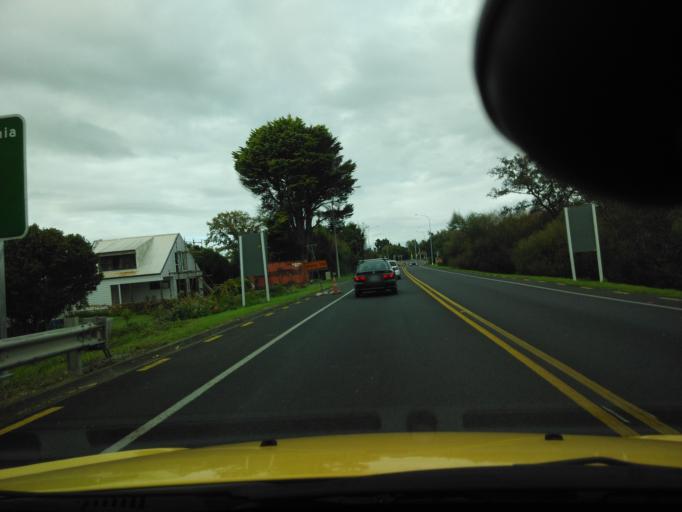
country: NZ
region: Waikato
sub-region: Waikato District
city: Ngaruawahia
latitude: -37.6094
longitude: 175.1854
